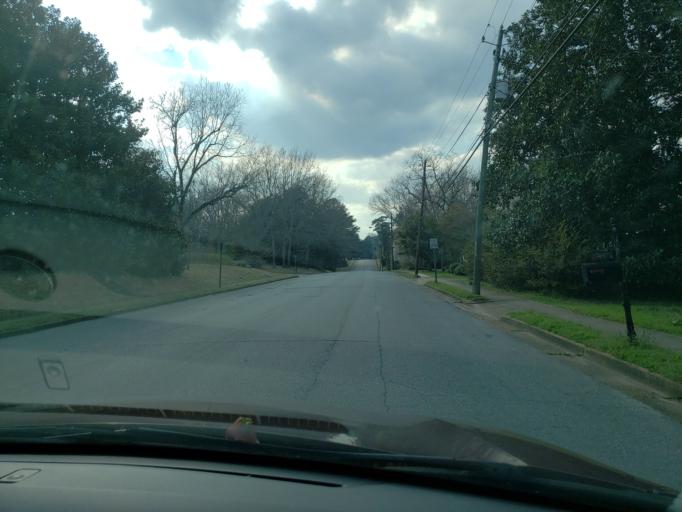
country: US
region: Alabama
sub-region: Hale County
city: Greensboro
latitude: 32.7042
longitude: -87.6016
